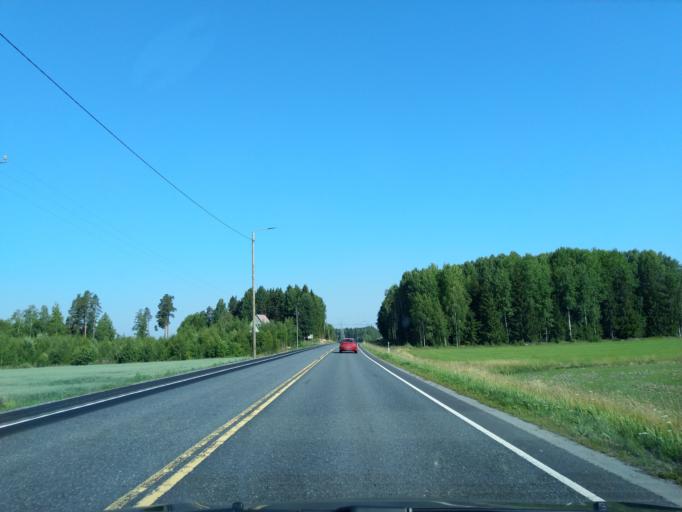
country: FI
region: Haeme
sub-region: Forssa
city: Forssa
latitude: 60.7693
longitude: 23.6810
